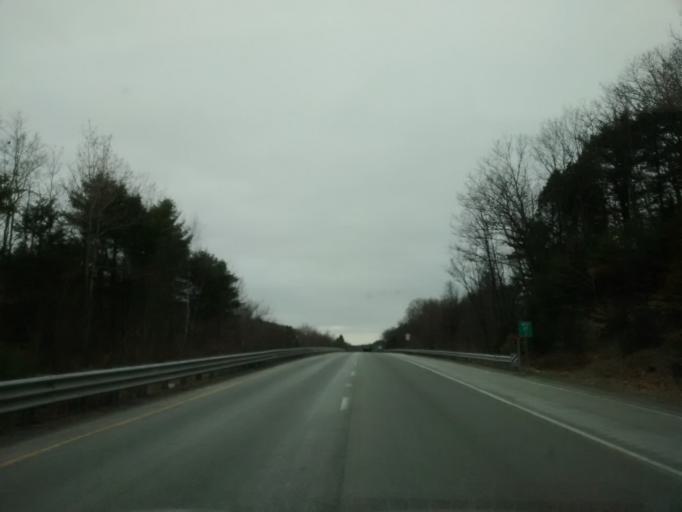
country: US
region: Massachusetts
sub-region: Worcester County
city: Westminster
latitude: 42.5602
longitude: -71.9413
